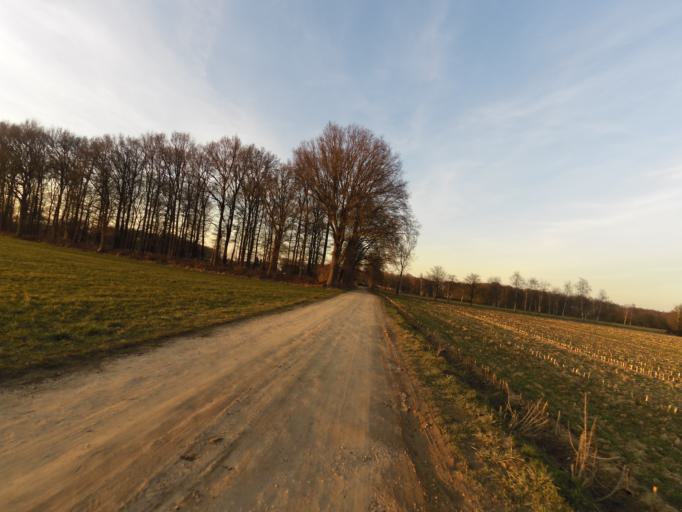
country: NL
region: Gelderland
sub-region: Gemeente Zevenaar
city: Zevenaar
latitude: 51.9435
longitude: 6.1010
